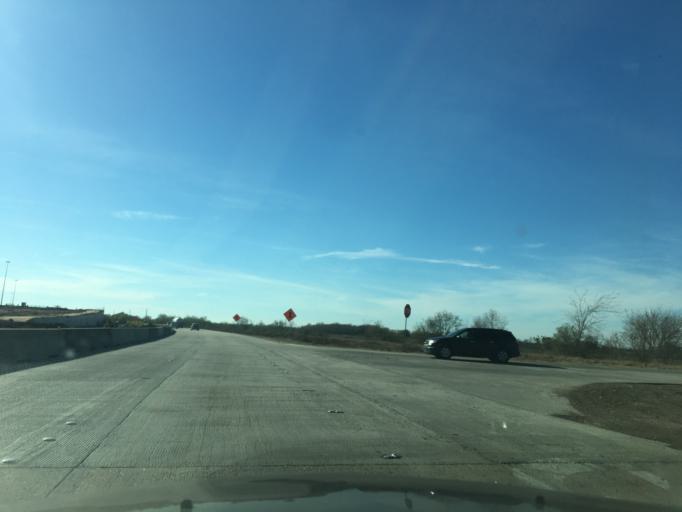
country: US
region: Texas
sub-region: Fort Bend County
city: Rosenberg
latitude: 29.5349
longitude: -95.8564
